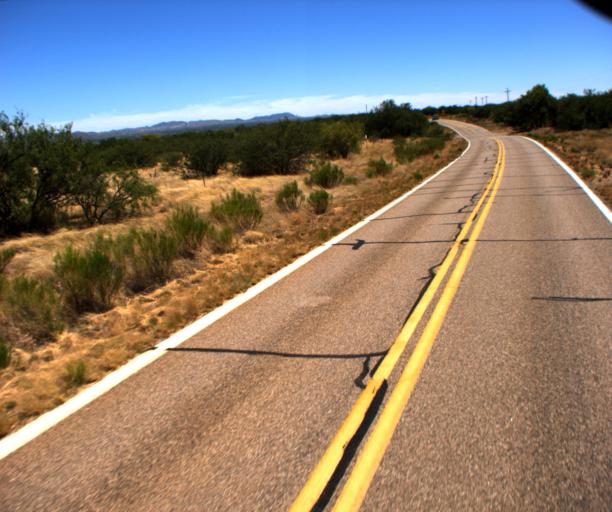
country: US
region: Arizona
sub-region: Pima County
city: Three Points
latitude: 31.6888
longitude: -111.4876
